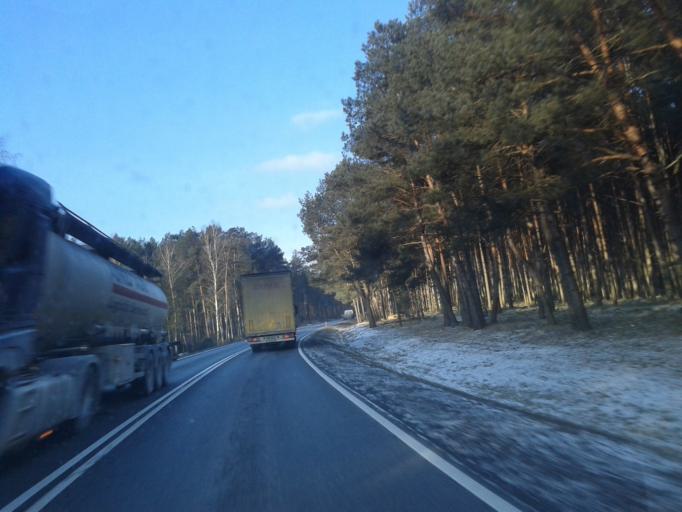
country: PL
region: Kujawsko-Pomorskie
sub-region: Bydgoszcz
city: Bydgoszcz
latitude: 53.0487
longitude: 18.0344
